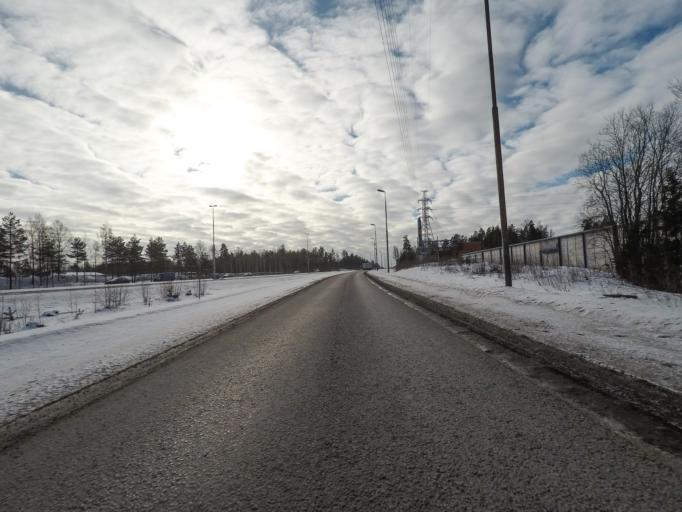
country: FI
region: Uusimaa
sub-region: Helsinki
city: Vantaa
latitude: 60.3045
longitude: 25.0973
